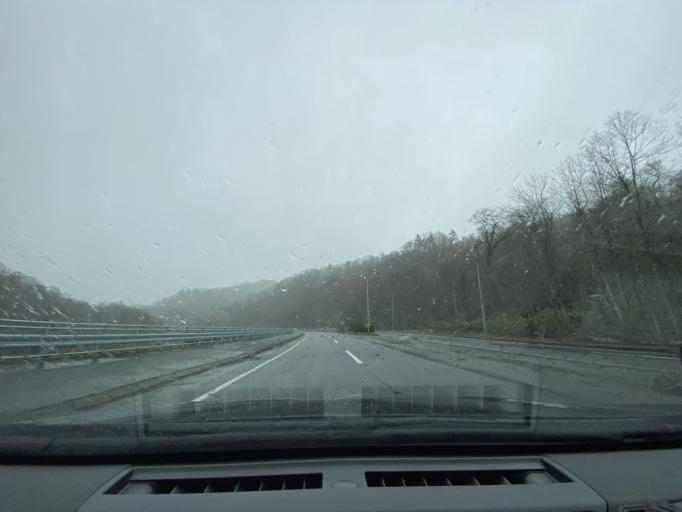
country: JP
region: Hokkaido
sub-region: Asahikawa-shi
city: Asahikawa
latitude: 43.7263
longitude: 142.2139
